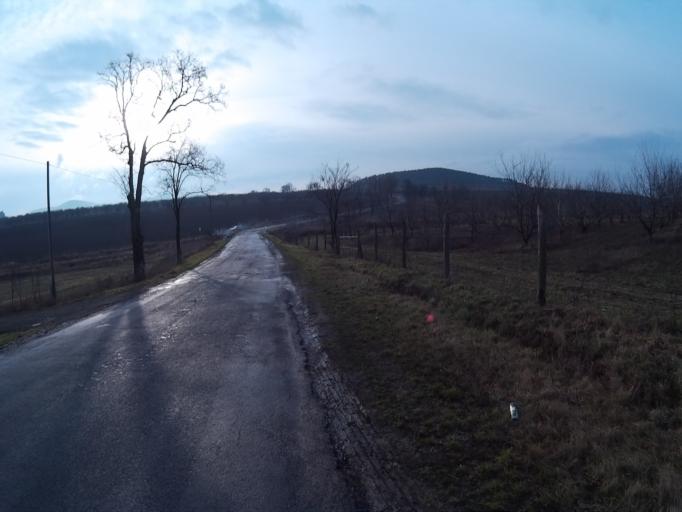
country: HU
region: Borsod-Abauj-Zemplen
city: Abaujszanto
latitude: 48.3460
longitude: 21.2132
